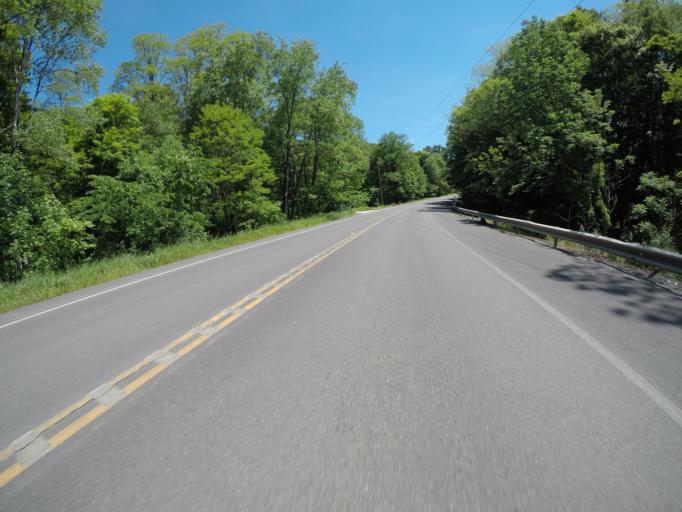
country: US
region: New York
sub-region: Delaware County
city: Walton
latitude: 42.1678
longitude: -75.0410
